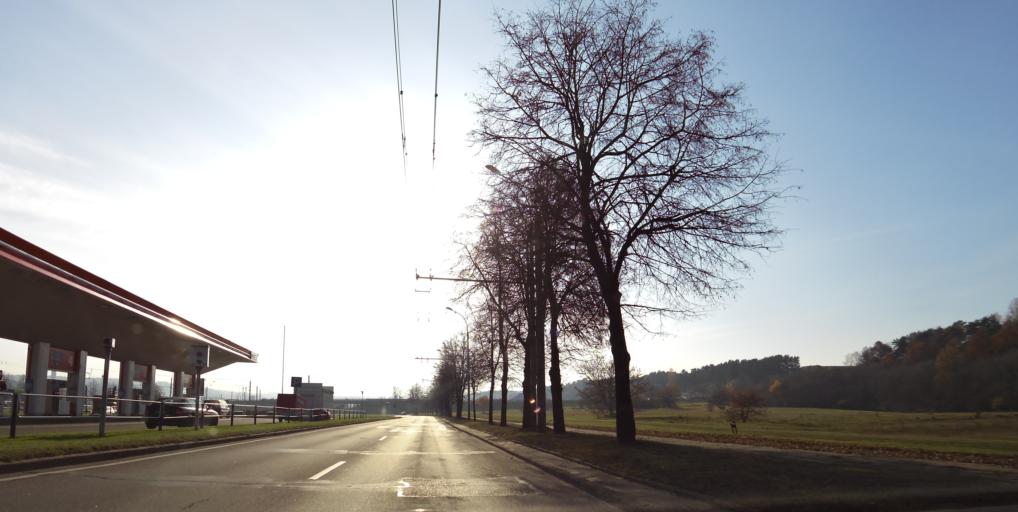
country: LT
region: Vilnius County
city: Lazdynai
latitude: 54.6746
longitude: 25.2224
